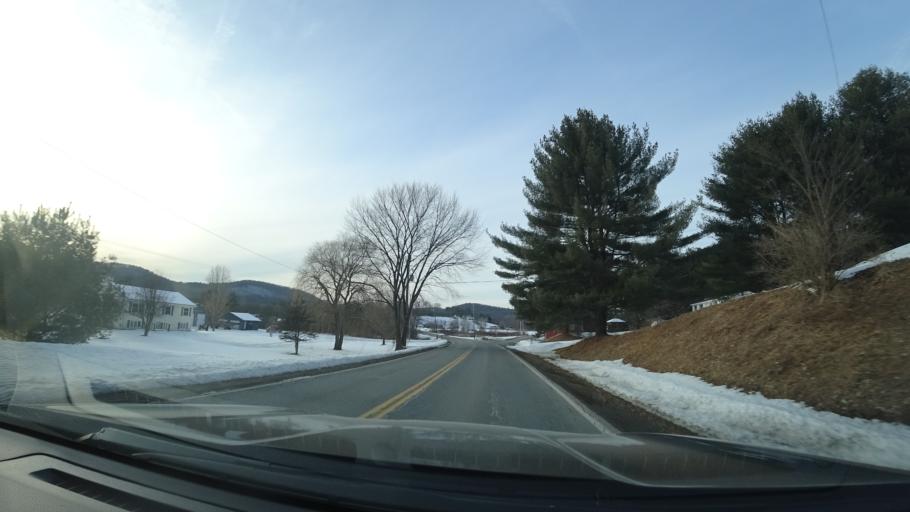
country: US
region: New York
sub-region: Washington County
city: Cambridge
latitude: 43.1709
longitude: -73.3523
